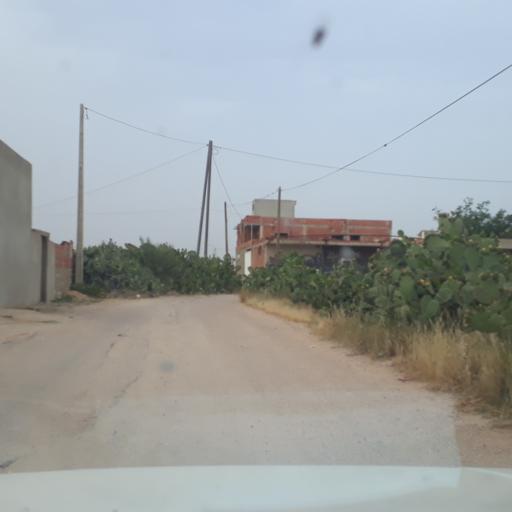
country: TN
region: Safaqis
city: Al Qarmadah
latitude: 34.8254
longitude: 10.7770
